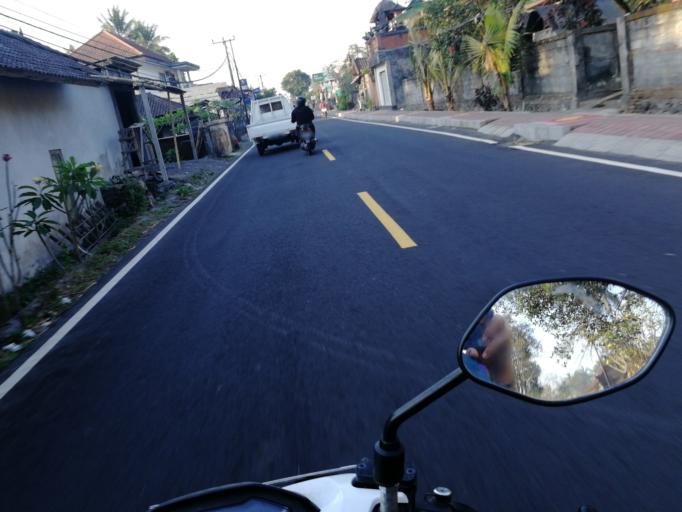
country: ID
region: Bali
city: Tistagede
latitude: -8.3823
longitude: 115.6077
